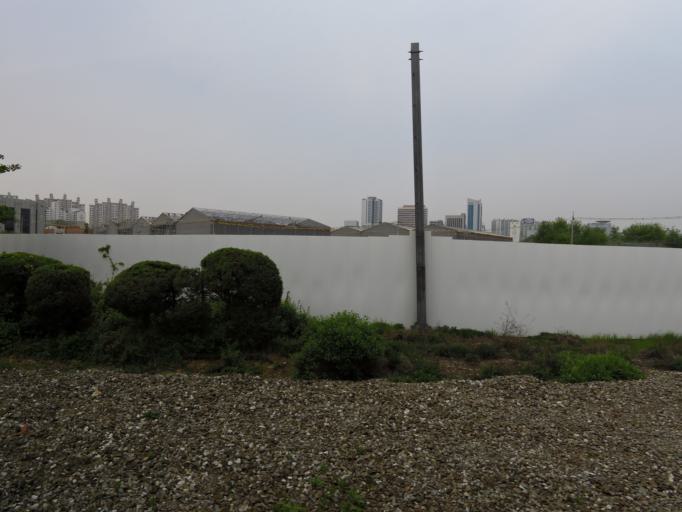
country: KR
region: Seoul
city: Seoul
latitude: 37.5274
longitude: 126.9609
